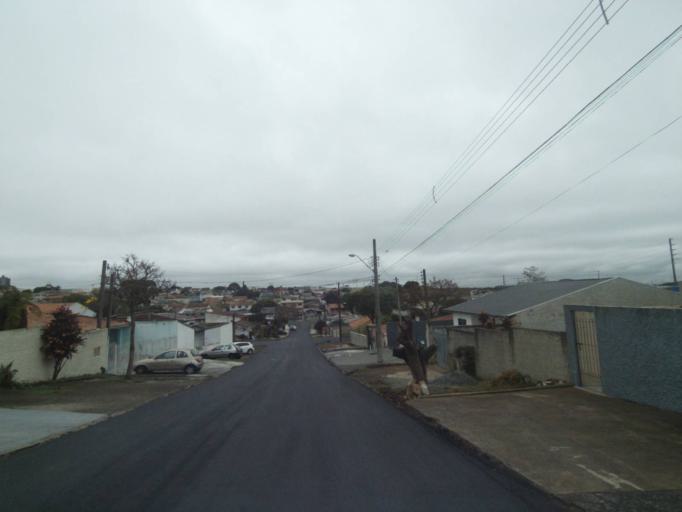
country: BR
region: Parana
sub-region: Curitiba
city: Curitiba
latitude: -25.5054
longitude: -49.3037
